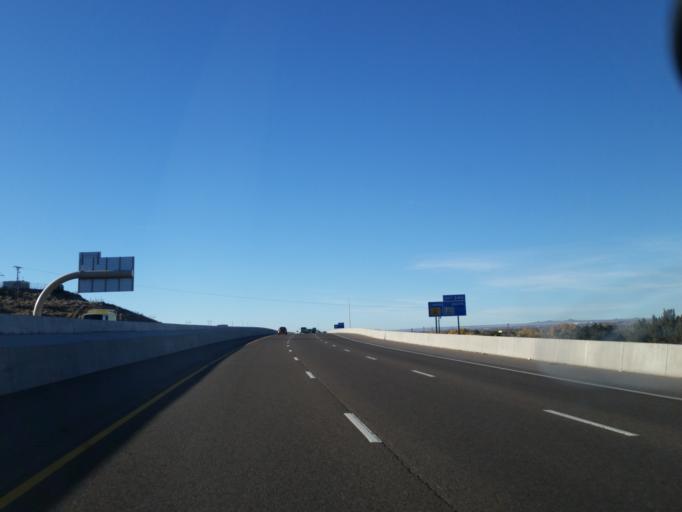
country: US
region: New Mexico
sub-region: Sandoval County
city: Bernalillo
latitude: 35.3048
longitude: -106.5366
